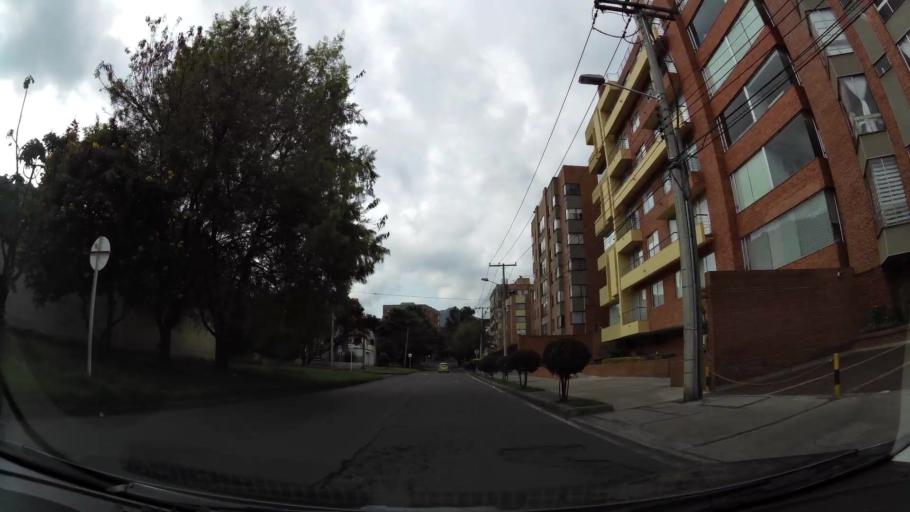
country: CO
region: Bogota D.C.
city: Barrio San Luis
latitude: 4.7095
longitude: -74.0302
